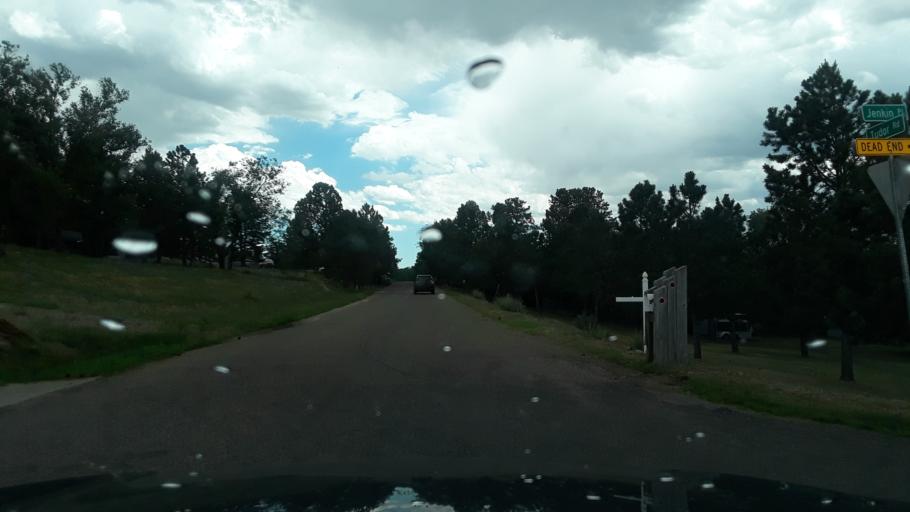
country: US
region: Colorado
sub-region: El Paso County
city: Air Force Academy
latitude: 38.9430
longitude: -104.8191
